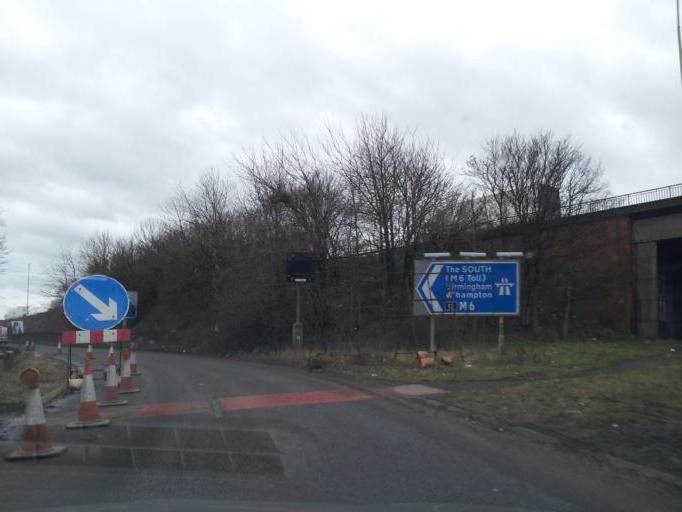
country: GB
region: England
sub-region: Staffordshire
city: Penkridge
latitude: 52.7637
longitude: -2.1069
